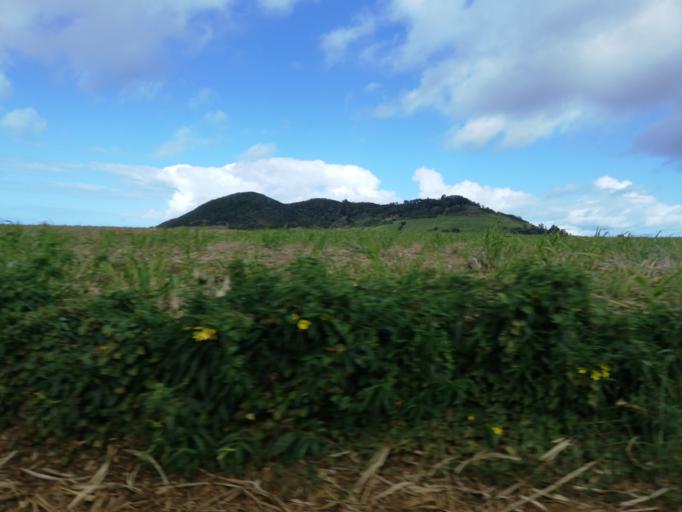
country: MU
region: Flacq
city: Grande Riviere Sud Est
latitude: -20.2821
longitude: 57.7565
